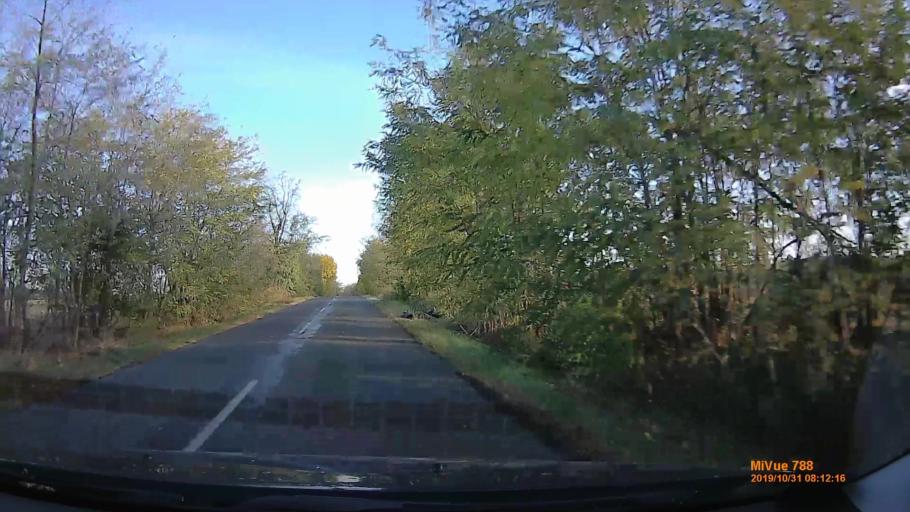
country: HU
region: Pest
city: Pilis
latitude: 47.3233
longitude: 19.5663
